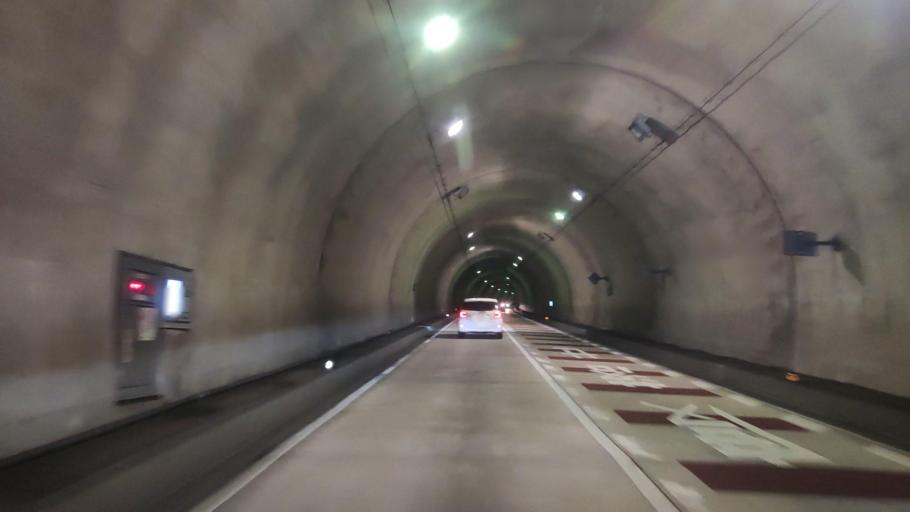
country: JP
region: Nara
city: Yoshino-cho
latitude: 34.2063
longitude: 135.9977
